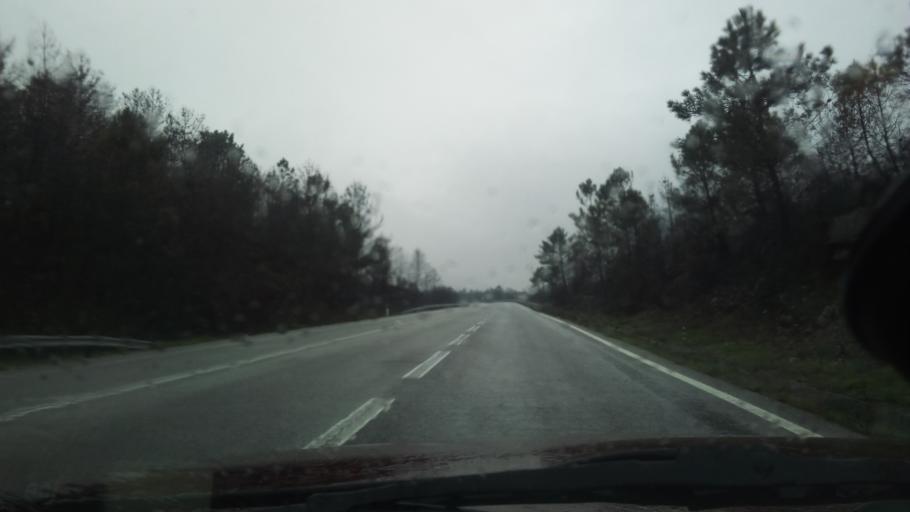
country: PT
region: Guarda
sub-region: Fornos de Algodres
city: Fornos de Algodres
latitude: 40.6132
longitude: -7.5958
